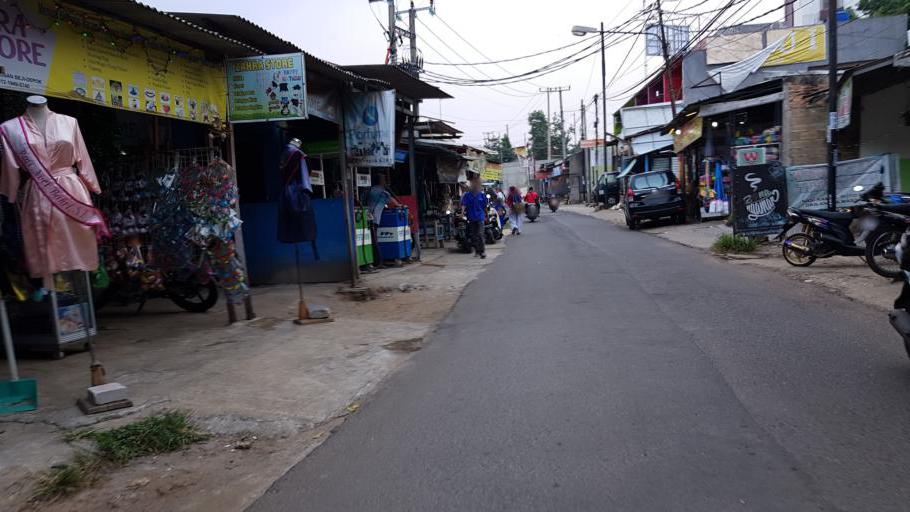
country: ID
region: West Java
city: Depok
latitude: -6.3691
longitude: 106.8177
